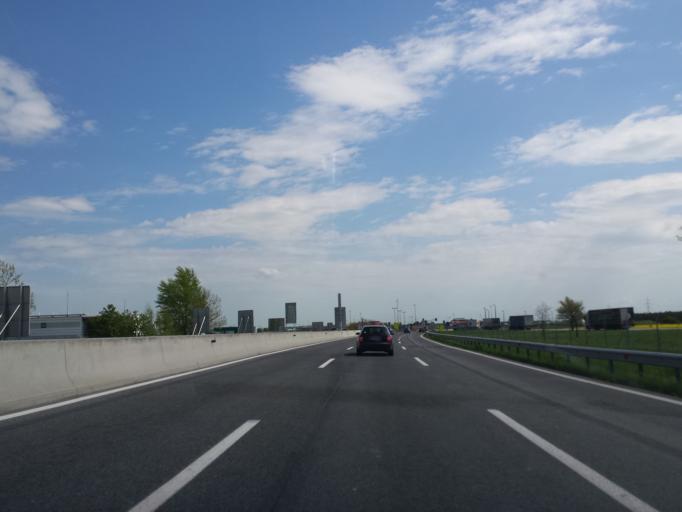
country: AT
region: Burgenland
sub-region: Politischer Bezirk Neusiedl am See
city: Nickelsdorf
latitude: 47.9259
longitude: 17.1093
